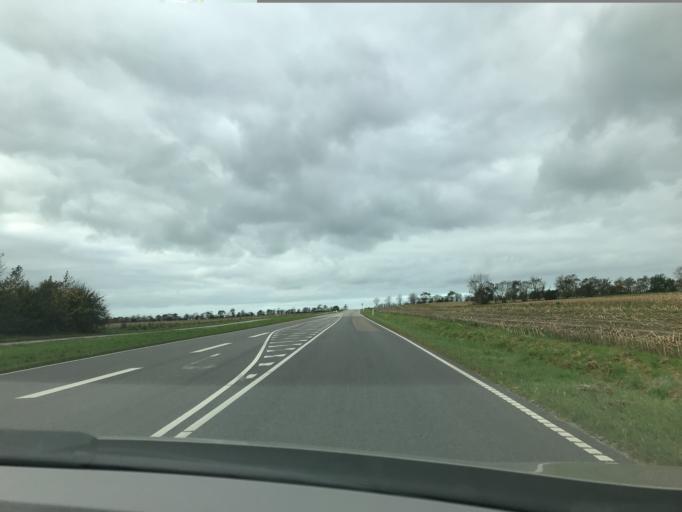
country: DK
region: South Denmark
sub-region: Varde Kommune
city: Olgod
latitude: 55.7938
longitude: 8.6643
